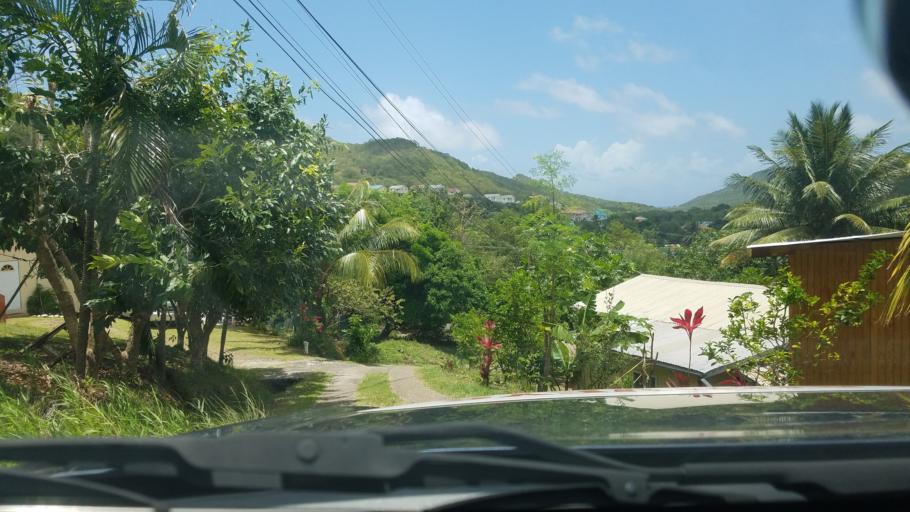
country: LC
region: Gros-Islet
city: Gros Islet
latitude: 14.0549
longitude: -60.9331
